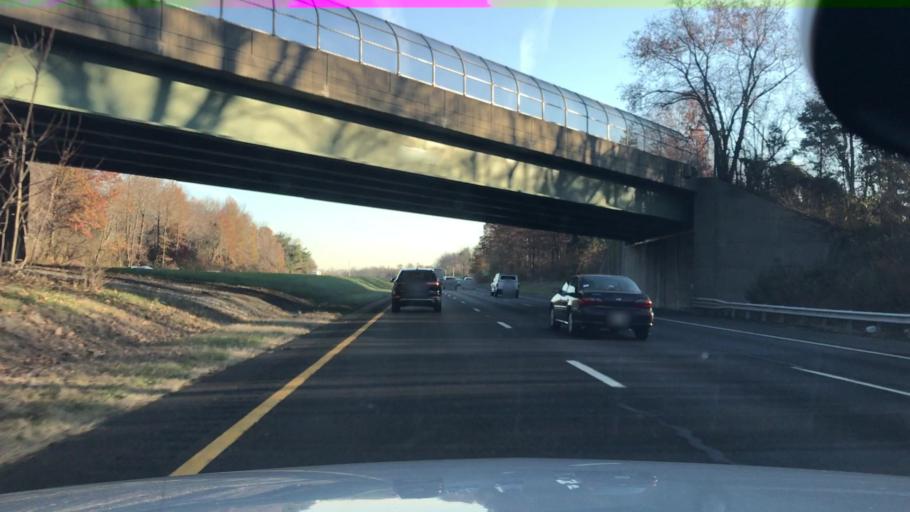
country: US
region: New Jersey
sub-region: Burlington County
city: Roebling
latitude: 40.0792
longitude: -74.7679
